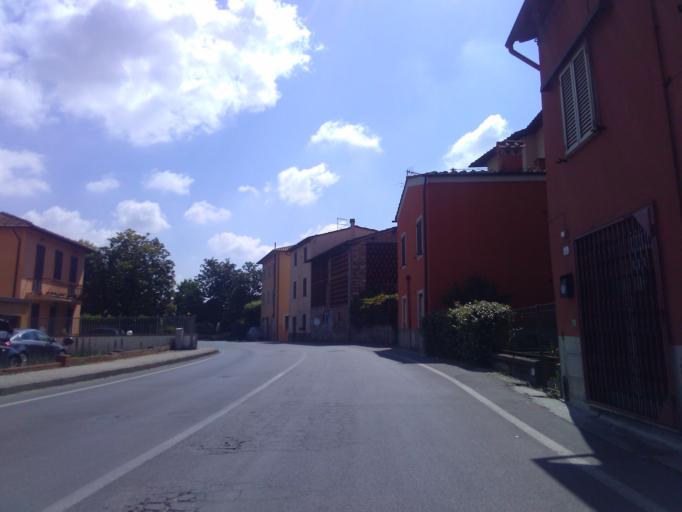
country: IT
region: Tuscany
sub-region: Provincia di Lucca
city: Lucca
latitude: 43.8412
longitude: 10.4818
